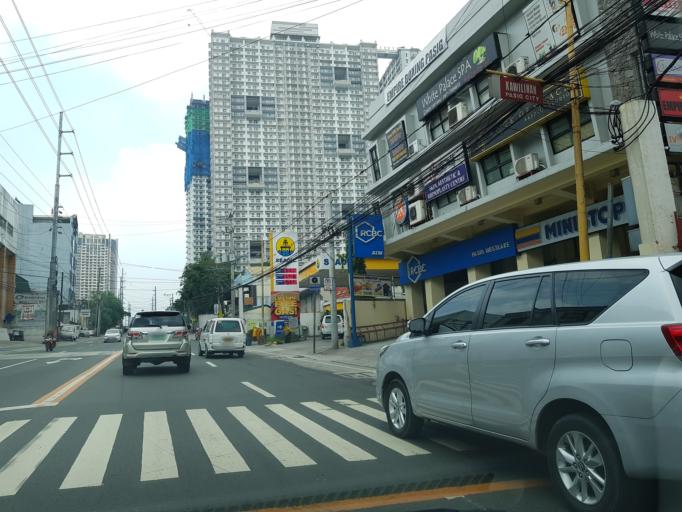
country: PH
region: Metro Manila
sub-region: Pasig
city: Pasig City
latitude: 14.5675
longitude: 121.0661
